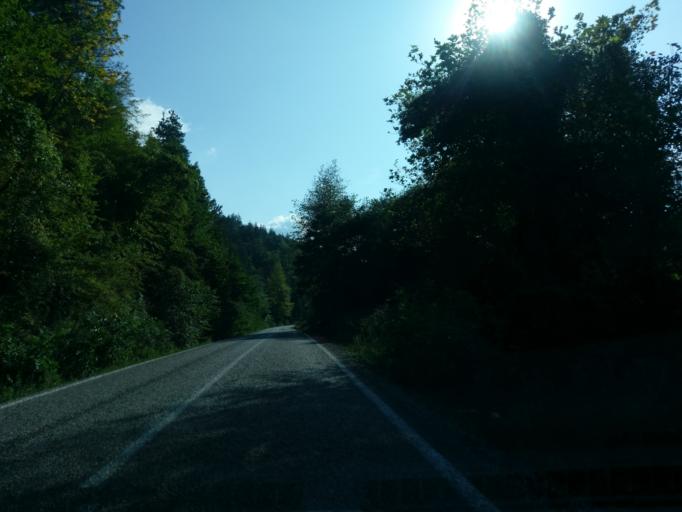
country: TR
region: Sinop
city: Yenikonak
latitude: 41.8837
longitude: 34.5639
